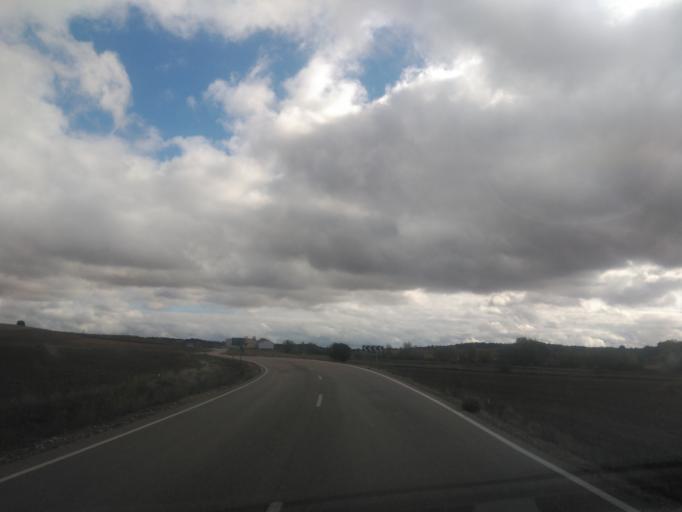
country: ES
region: Castille and Leon
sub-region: Provincia de Soria
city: Alcubilla de Avellaneda
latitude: 41.7226
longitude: -3.3181
